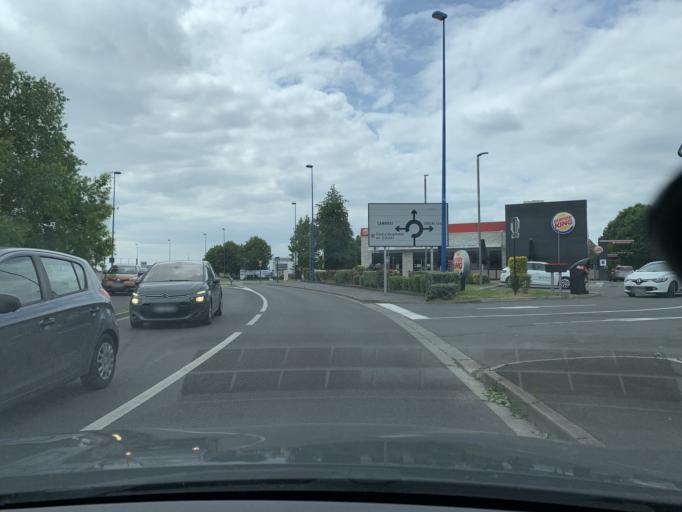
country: FR
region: Nord-Pas-de-Calais
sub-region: Departement du Nord
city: Lambres-lez-Douai
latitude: 50.3479
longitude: 3.0911
